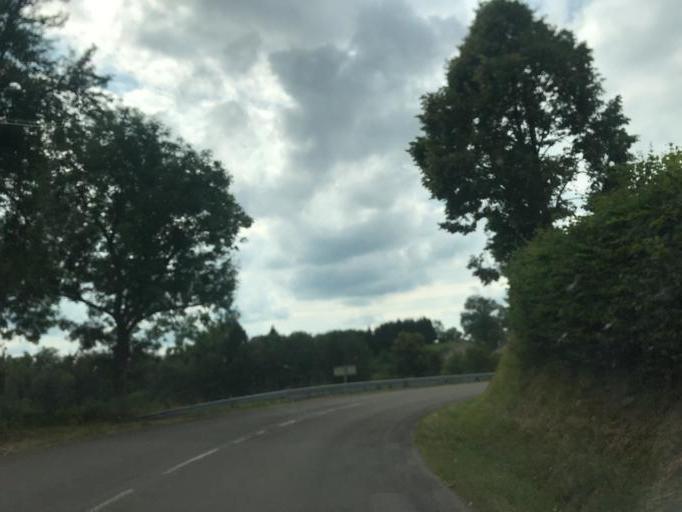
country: FR
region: Franche-Comte
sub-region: Departement du Jura
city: Longchaumois
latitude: 46.4980
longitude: 5.9006
